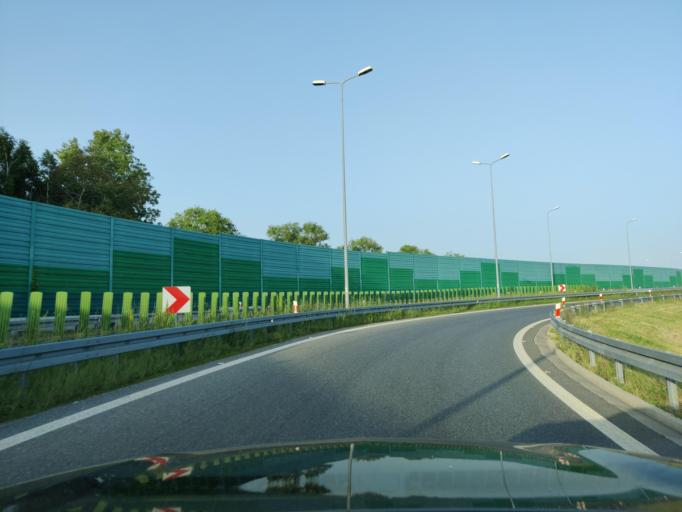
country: PL
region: Masovian Voivodeship
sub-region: Powiat minski
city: Minsk Mazowiecki
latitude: 52.2096
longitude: 21.5296
